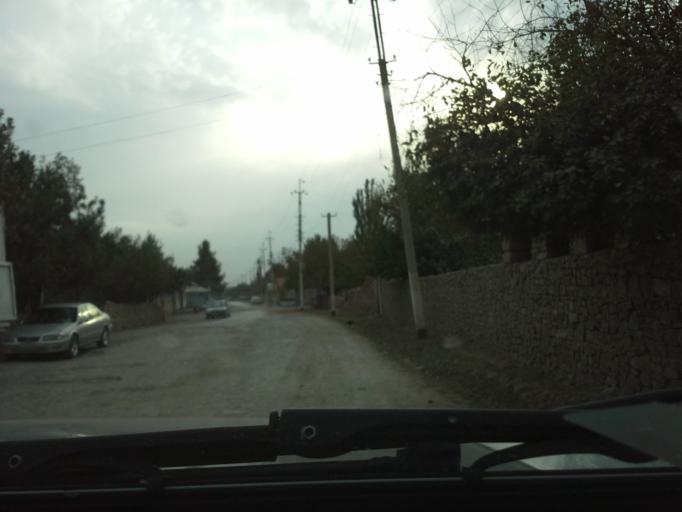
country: UZ
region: Qashqadaryo
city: Qorashina
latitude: 37.9189
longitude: 66.4856
